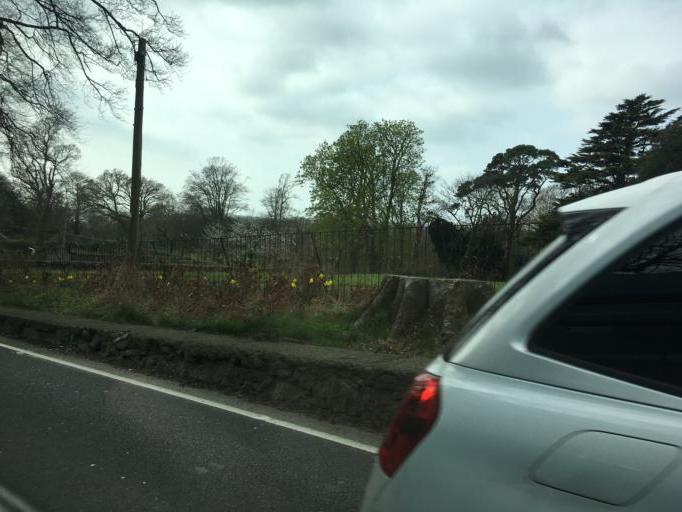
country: GB
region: Wales
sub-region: Gwynedd
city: Caernarfon
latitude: 53.1558
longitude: -4.2576
